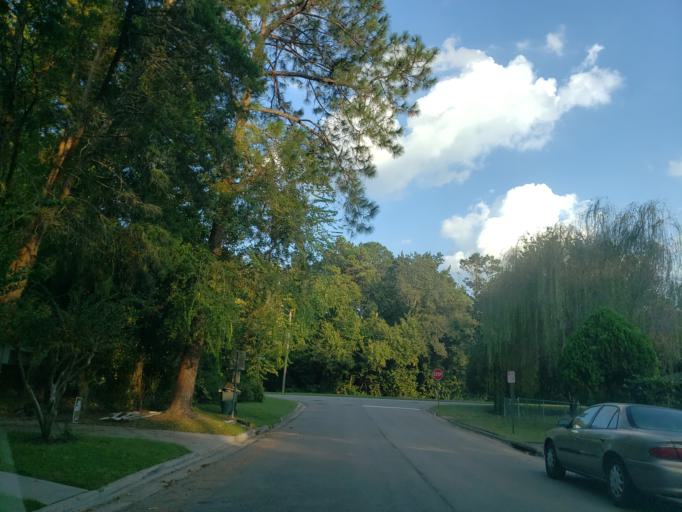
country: US
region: Georgia
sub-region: Chatham County
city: Thunderbolt
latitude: 32.0538
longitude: -81.0745
